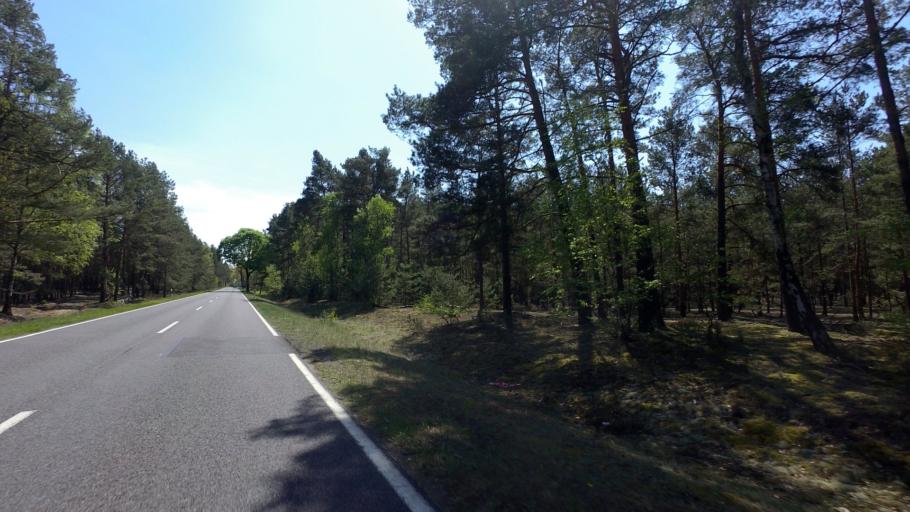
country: DE
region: Brandenburg
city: Halbe
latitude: 52.1580
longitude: 13.7374
